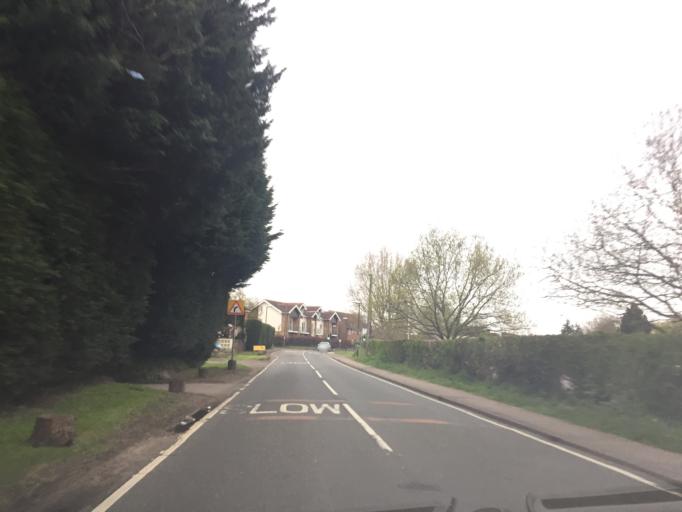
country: GB
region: England
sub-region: Essex
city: Theydon Bois
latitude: 51.6534
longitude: 0.1239
